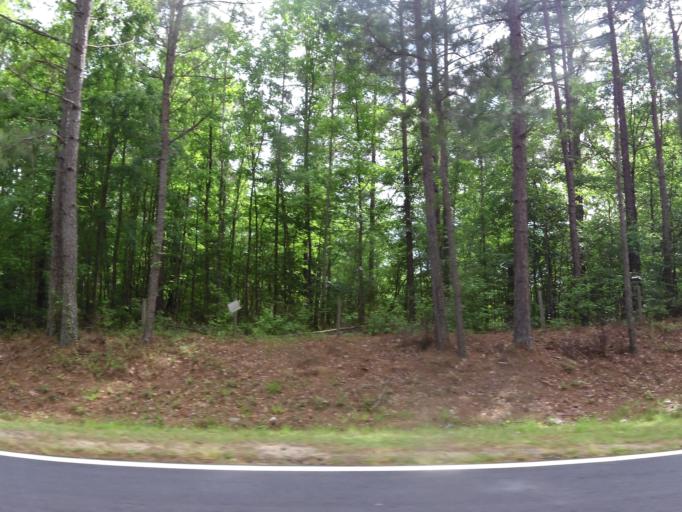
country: US
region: Georgia
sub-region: McDuffie County
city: Thomson
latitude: 33.5338
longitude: -82.4890
